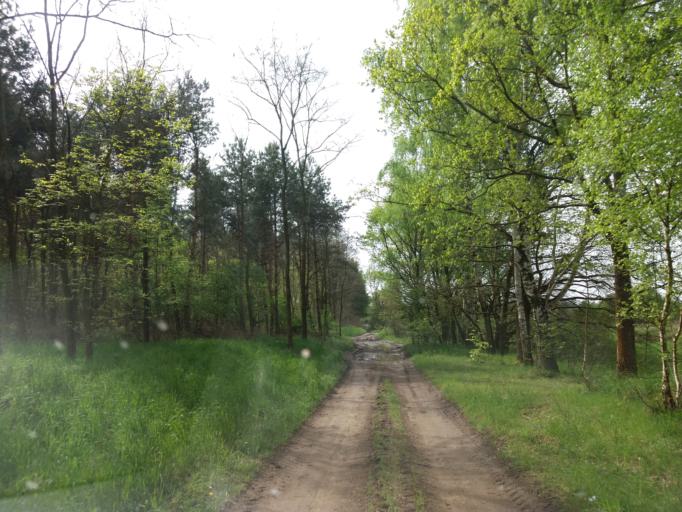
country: PL
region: West Pomeranian Voivodeship
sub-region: Powiat choszczenski
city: Krzecin
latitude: 53.0035
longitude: 15.5514
